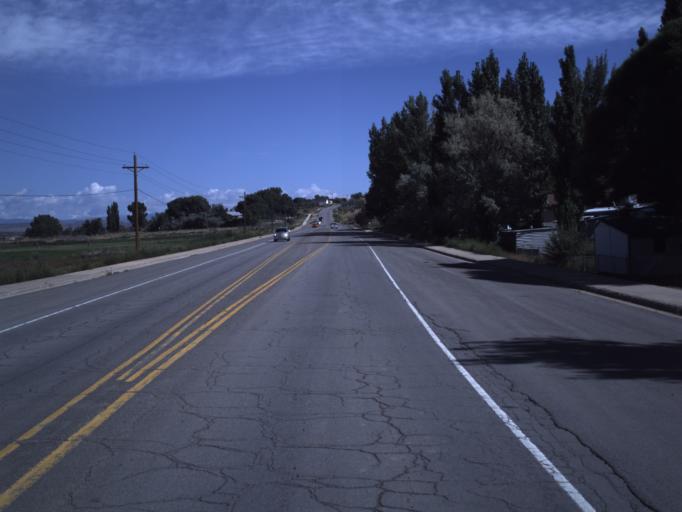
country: US
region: Utah
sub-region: Duchesne County
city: Duchesne
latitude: 40.1696
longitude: -110.4013
